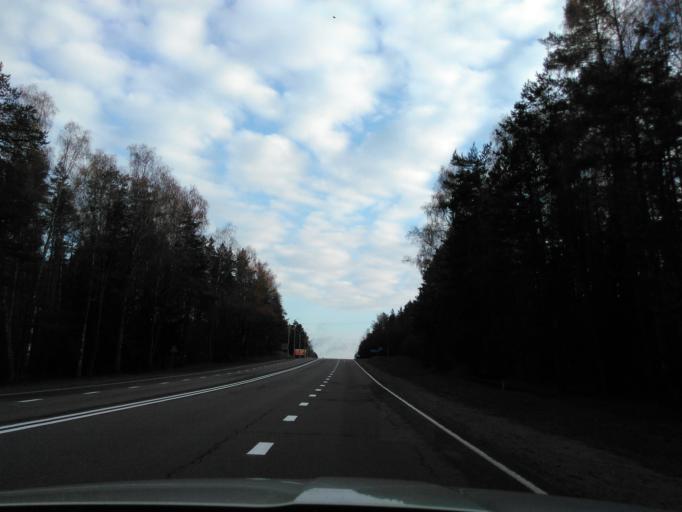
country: BY
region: Minsk
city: Plyeshchanitsy
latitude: 54.3254
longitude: 27.8754
